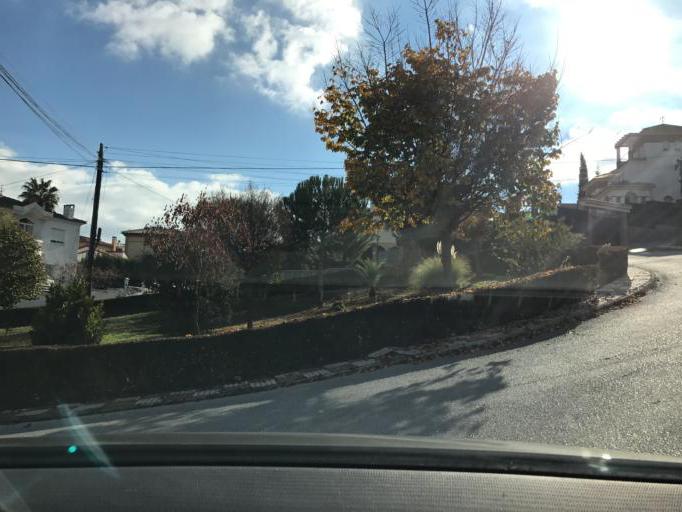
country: ES
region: Andalusia
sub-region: Provincia de Granada
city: Otura
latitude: 37.0855
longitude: -3.6291
